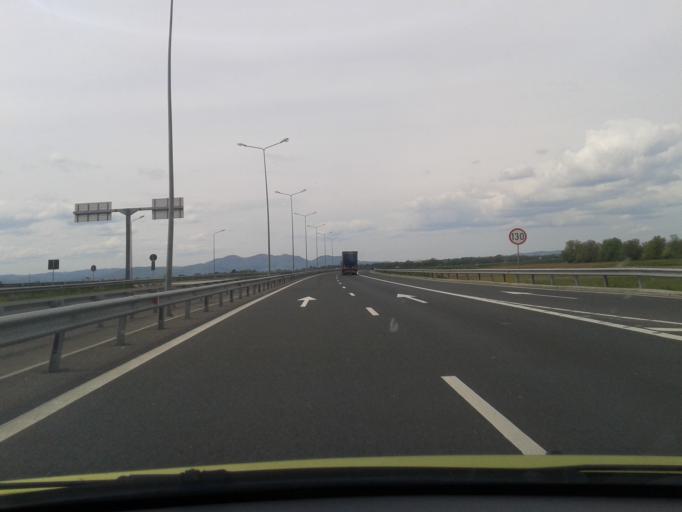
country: RO
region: Hunedoara
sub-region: Comuna Rapoltu Mare
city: Rapoltu Mare
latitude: 45.8498
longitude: 23.0458
